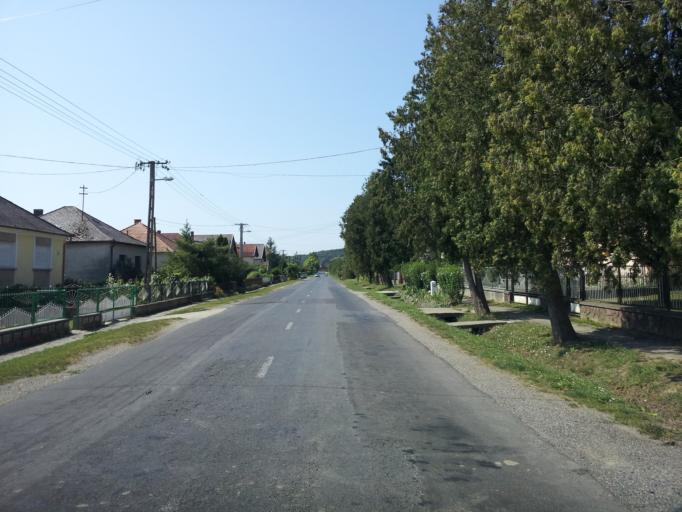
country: HU
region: Zala
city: Heviz
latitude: 46.8414
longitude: 17.0946
